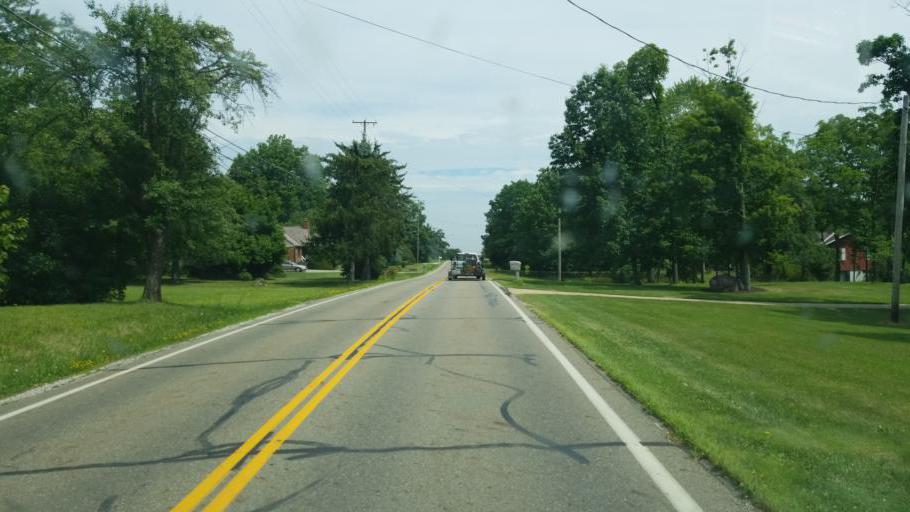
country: US
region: Ohio
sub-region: Summit County
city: Macedonia
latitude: 41.3342
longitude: -81.4792
